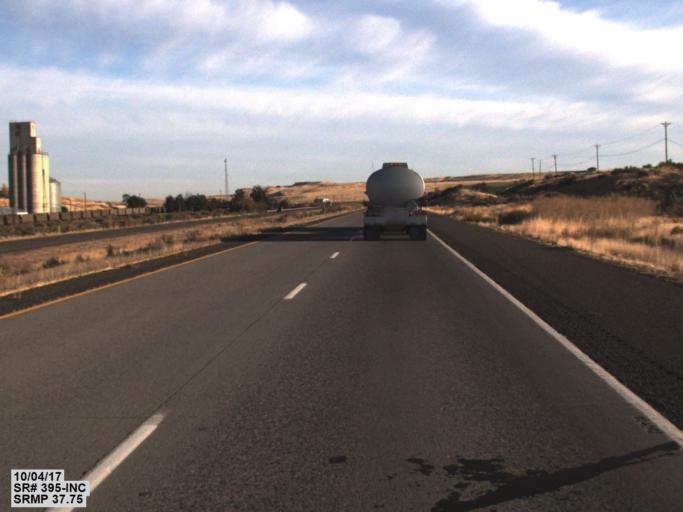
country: US
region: Washington
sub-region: Franklin County
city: Basin City
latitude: 46.4536
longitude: -119.0154
